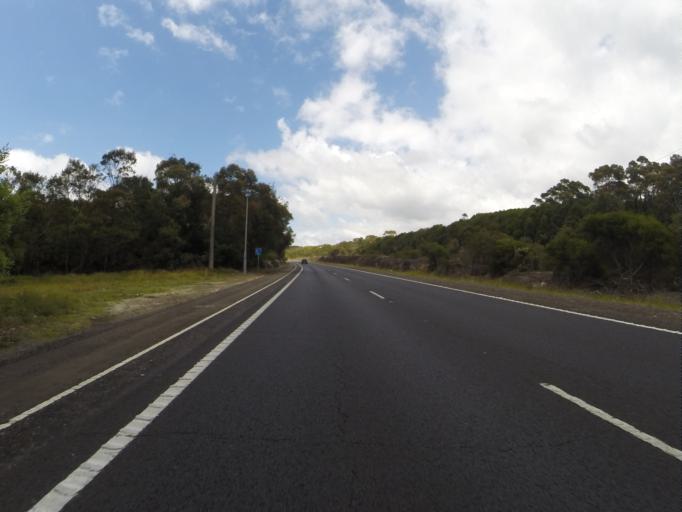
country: AU
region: New South Wales
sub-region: Wollongong
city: Helensburgh
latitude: -34.2278
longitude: 150.9485
